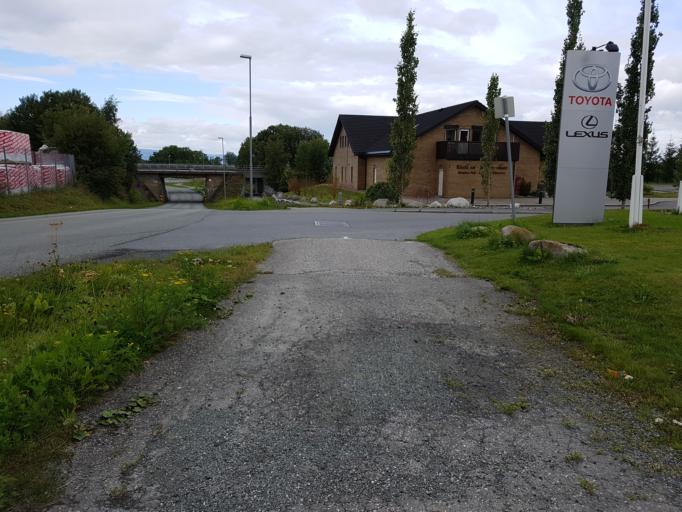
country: NO
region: Sor-Trondelag
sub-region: Trondheim
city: Trondheim
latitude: 63.4353
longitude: 10.4692
